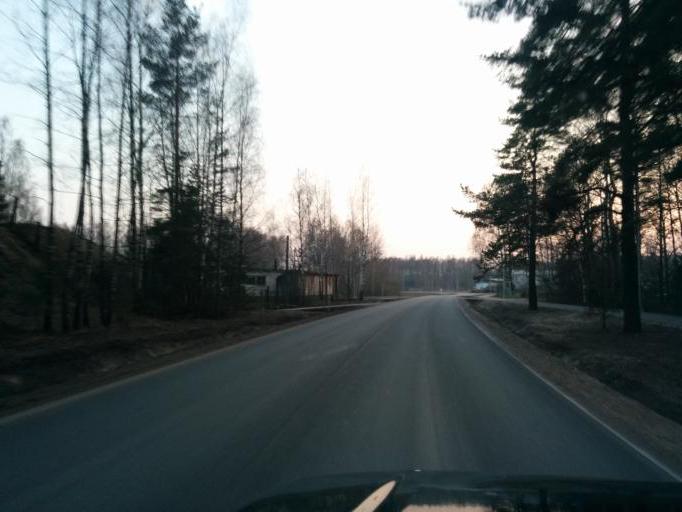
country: LV
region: Kekava
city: Balozi
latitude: 56.8701
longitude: 24.1098
